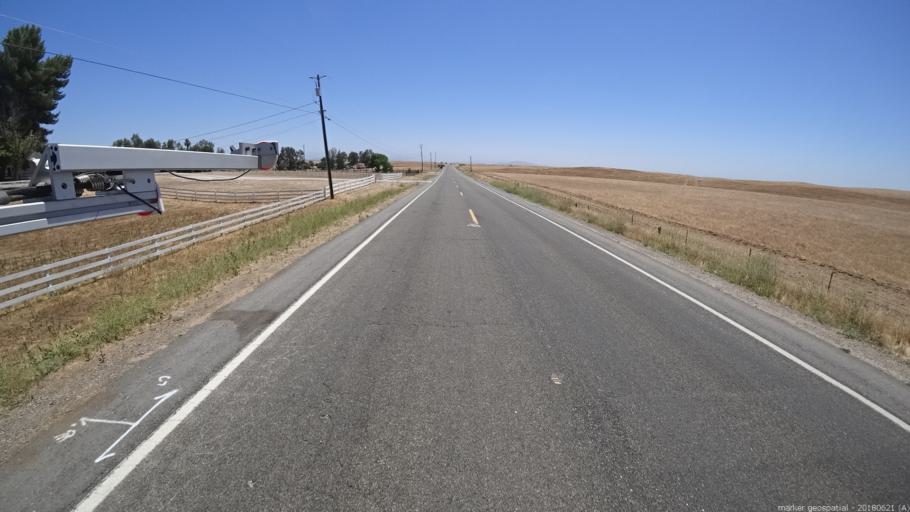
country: US
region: California
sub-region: Madera County
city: Bonadelle Ranchos-Madera Ranchos
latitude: 36.9666
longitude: -119.8793
